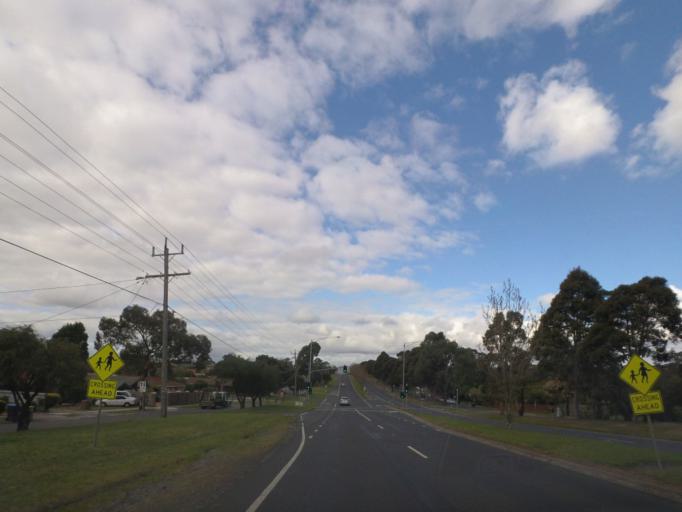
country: AU
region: Victoria
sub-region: Knox
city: Wantirna
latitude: -37.8463
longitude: 145.2353
